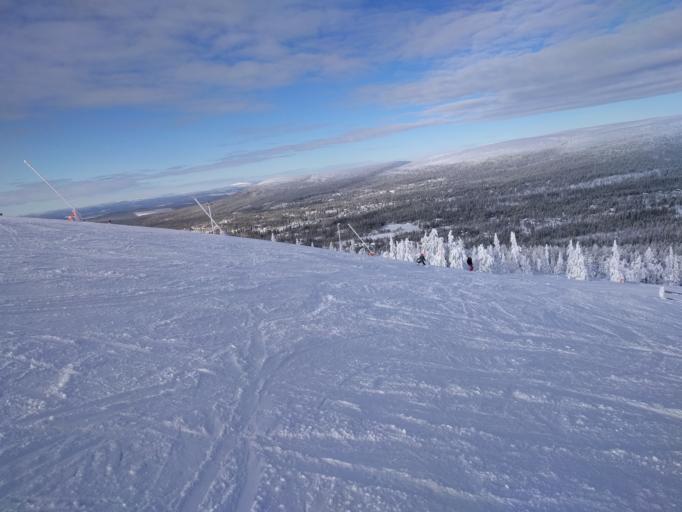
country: NO
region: Hedmark
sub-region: Trysil
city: Innbygda
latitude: 61.1770
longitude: 13.0165
